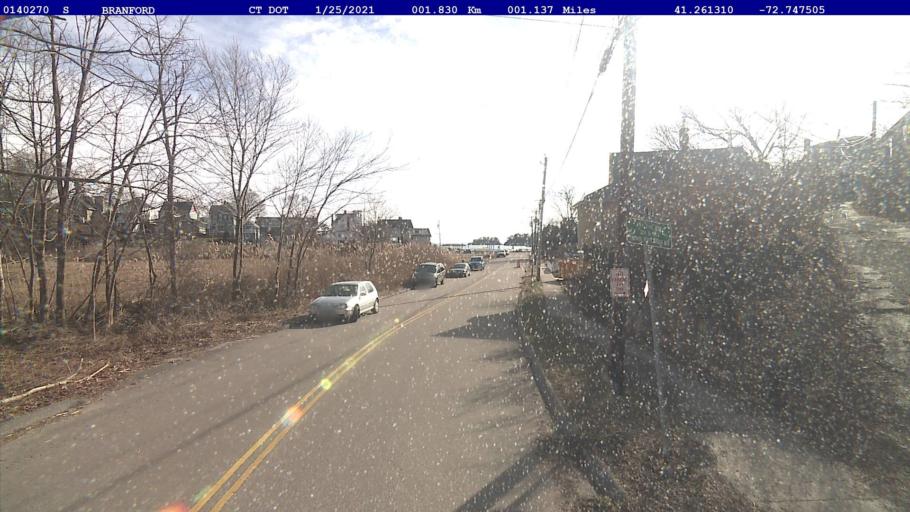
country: US
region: Connecticut
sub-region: New Haven County
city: North Branford
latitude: 41.2612
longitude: -72.7476
